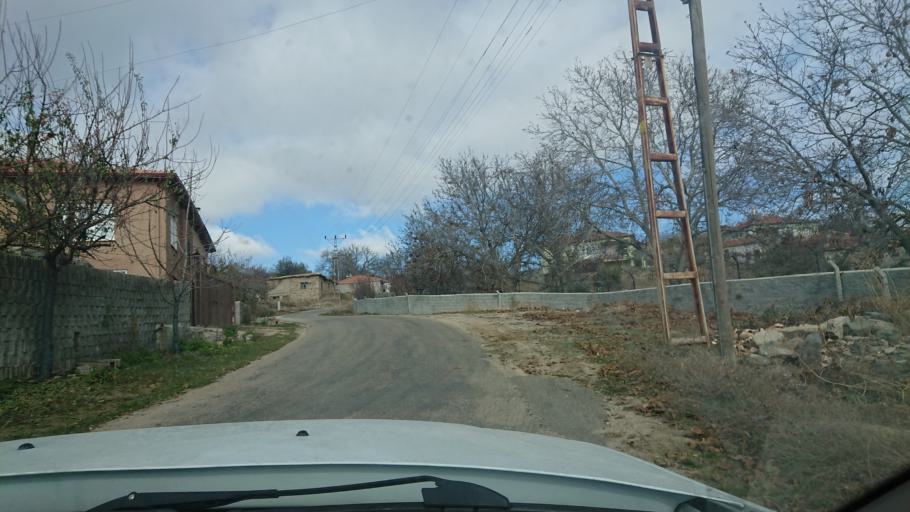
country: TR
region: Aksaray
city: Agacoren
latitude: 38.8213
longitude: 33.9588
